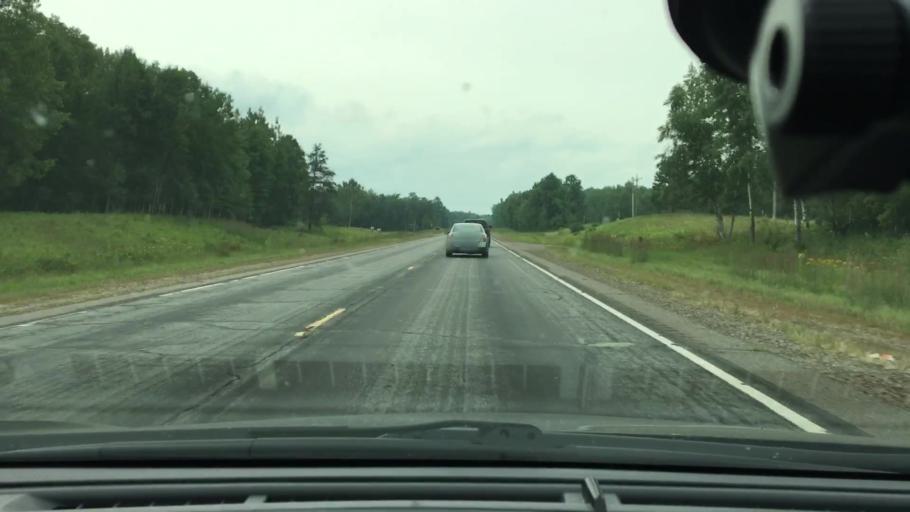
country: US
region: Minnesota
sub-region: Crow Wing County
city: Cross Lake
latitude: 46.6804
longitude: -93.9530
